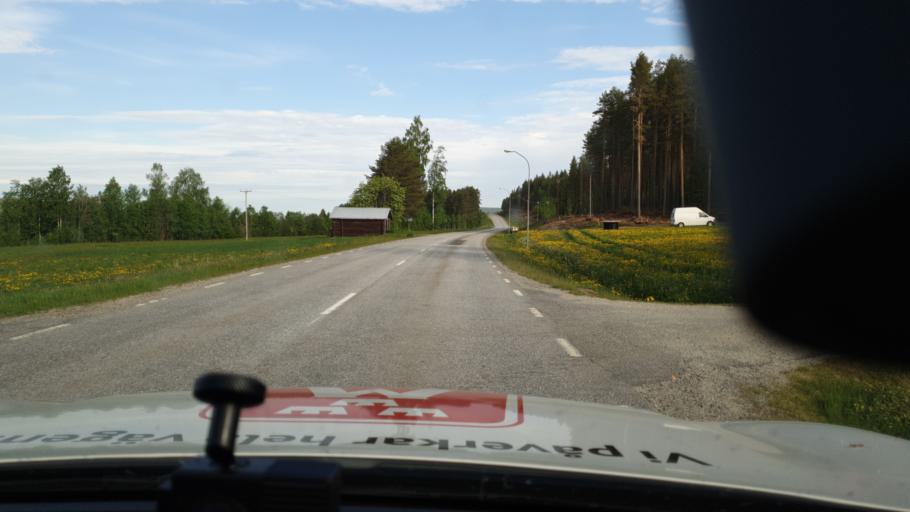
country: SE
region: Vaesterbotten
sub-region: Bjurholms Kommun
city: Bjurholm
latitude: 64.2635
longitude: 19.2779
